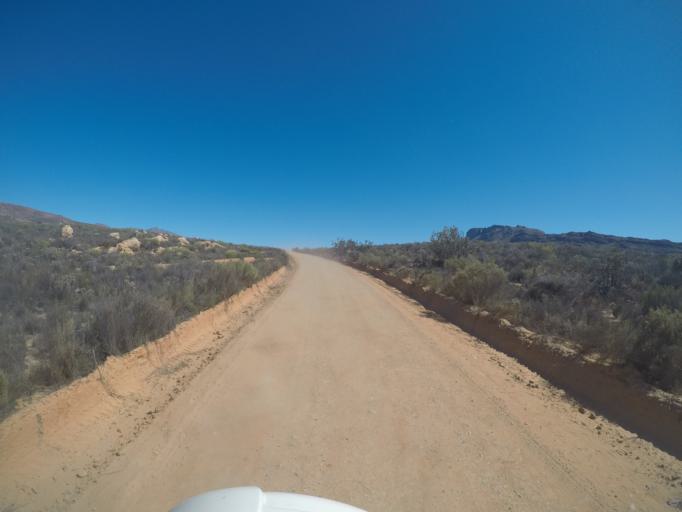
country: ZA
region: Western Cape
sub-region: West Coast District Municipality
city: Clanwilliam
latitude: -32.5062
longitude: 19.2984
